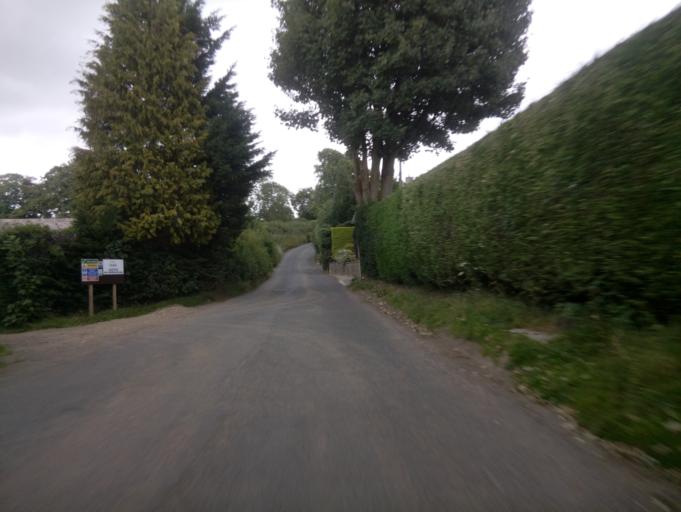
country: GB
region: England
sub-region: Gloucestershire
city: Shurdington
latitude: 51.8134
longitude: -2.1455
